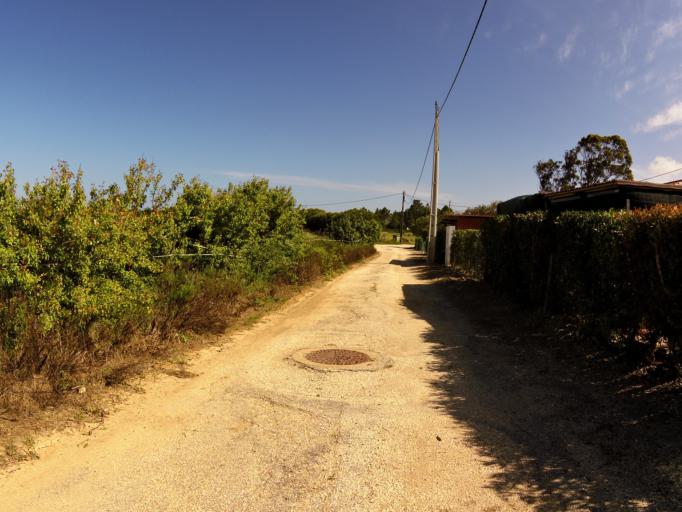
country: PT
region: Faro
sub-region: Aljezur
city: Aljezur
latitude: 37.3353
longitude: -8.8087
